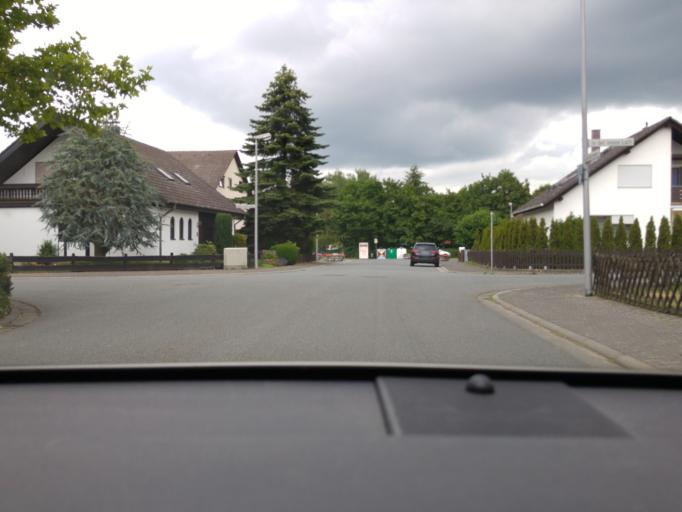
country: DE
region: Hesse
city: Dreieich
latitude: 50.0225
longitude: 8.7018
